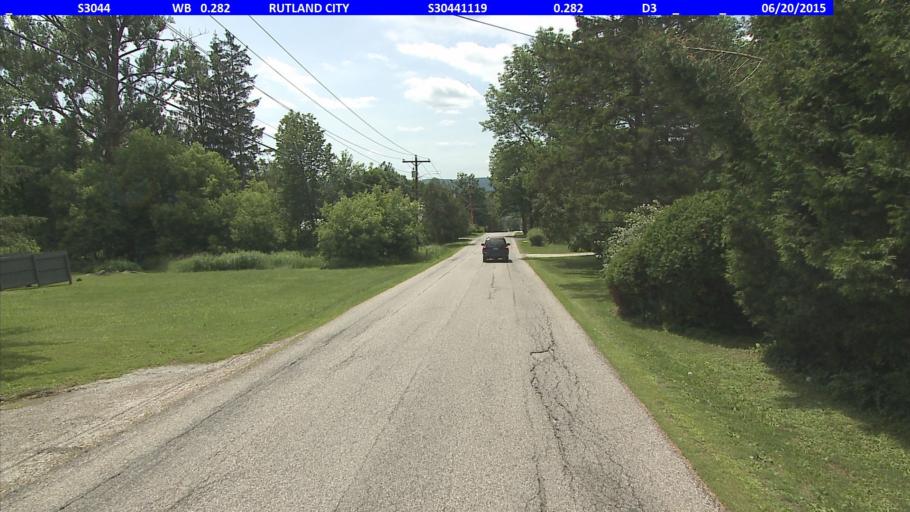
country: US
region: Vermont
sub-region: Rutland County
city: Rutland
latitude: 43.6194
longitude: -72.9686
